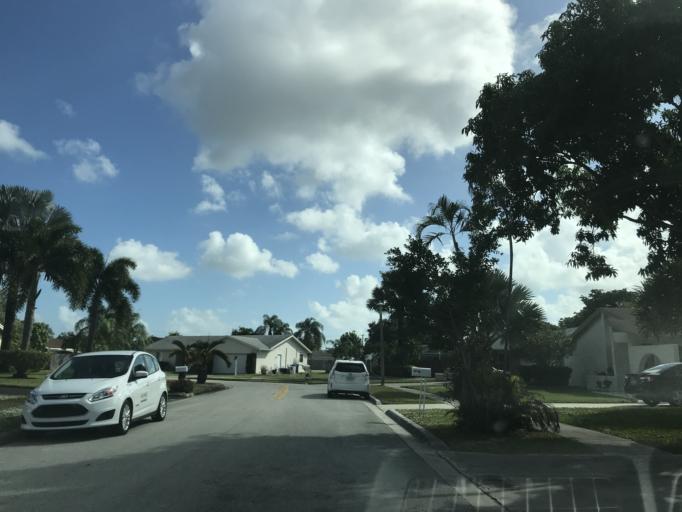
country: US
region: Florida
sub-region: Broward County
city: Coconut Creek
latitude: 26.2654
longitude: -80.1957
